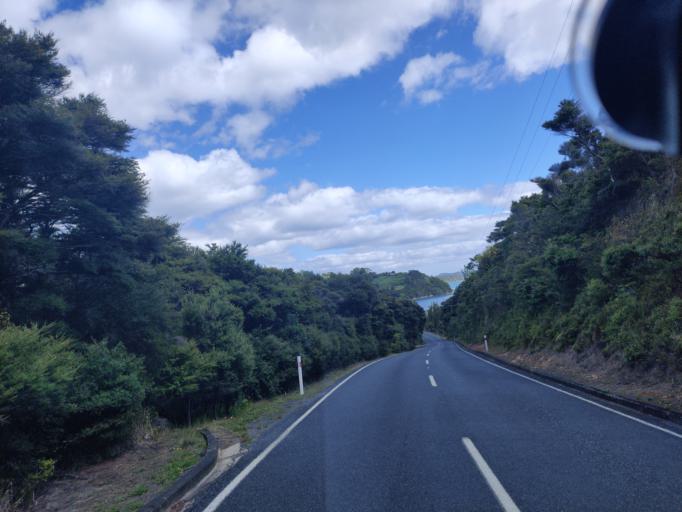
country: NZ
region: Northland
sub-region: Far North District
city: Paihia
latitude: -35.2617
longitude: 174.2584
